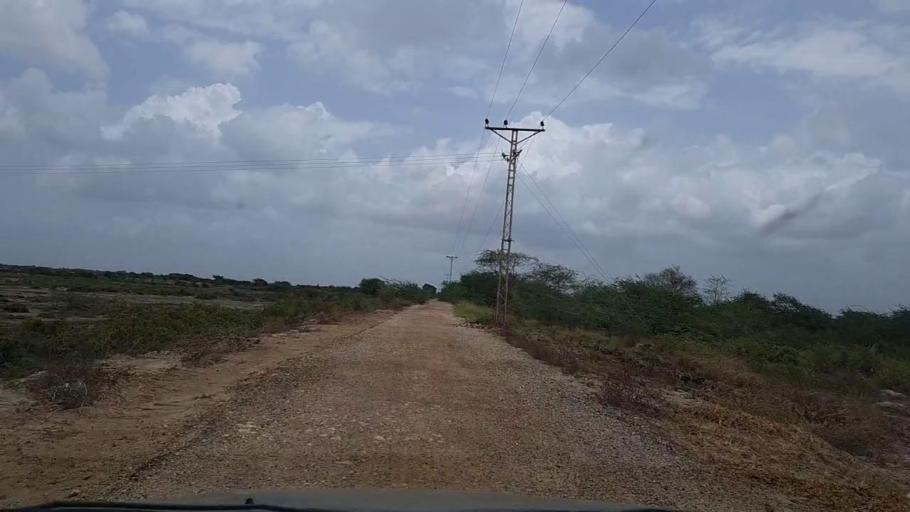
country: PK
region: Sindh
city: Thatta
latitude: 24.6131
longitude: 68.0302
